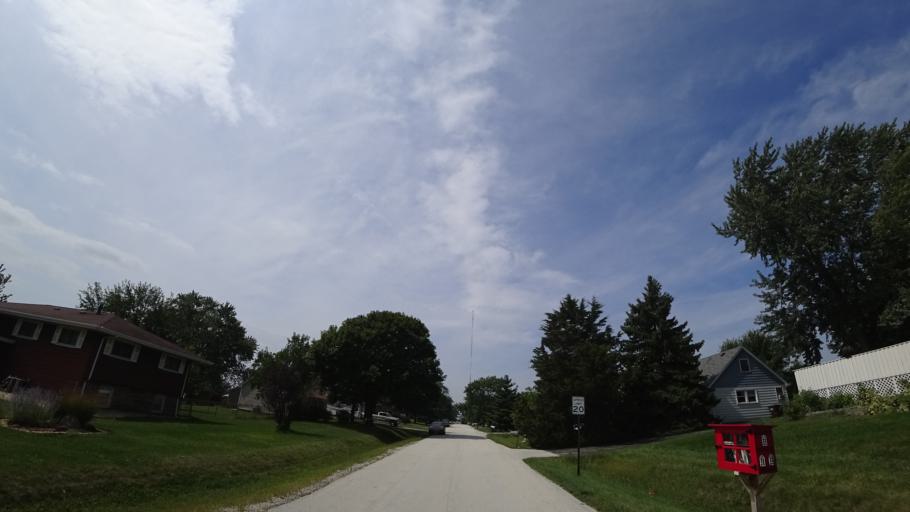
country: US
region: Illinois
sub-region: Cook County
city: Orland Hills
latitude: 41.5557
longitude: -87.8416
